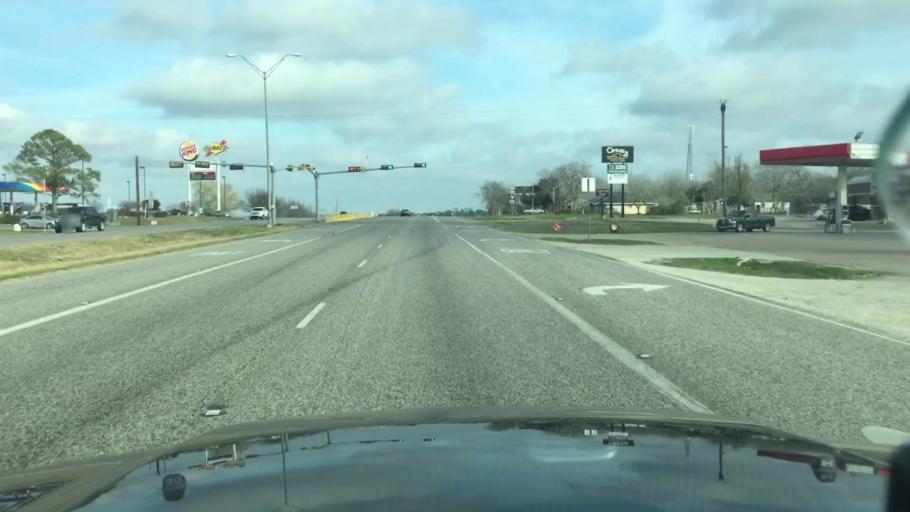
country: US
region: Texas
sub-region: Washington County
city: Brenham
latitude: 30.1351
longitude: -96.2579
